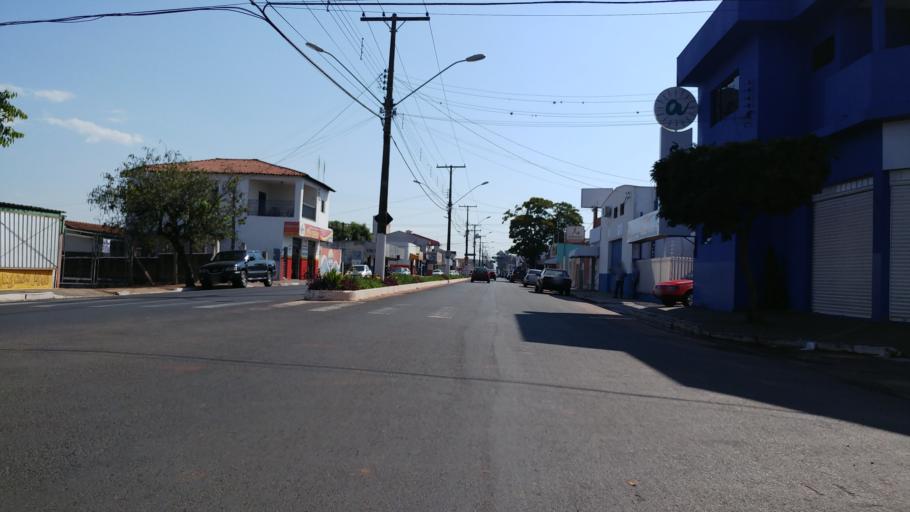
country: BR
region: Sao Paulo
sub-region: Paraguacu Paulista
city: Paraguacu Paulista
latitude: -22.4277
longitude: -50.5841
